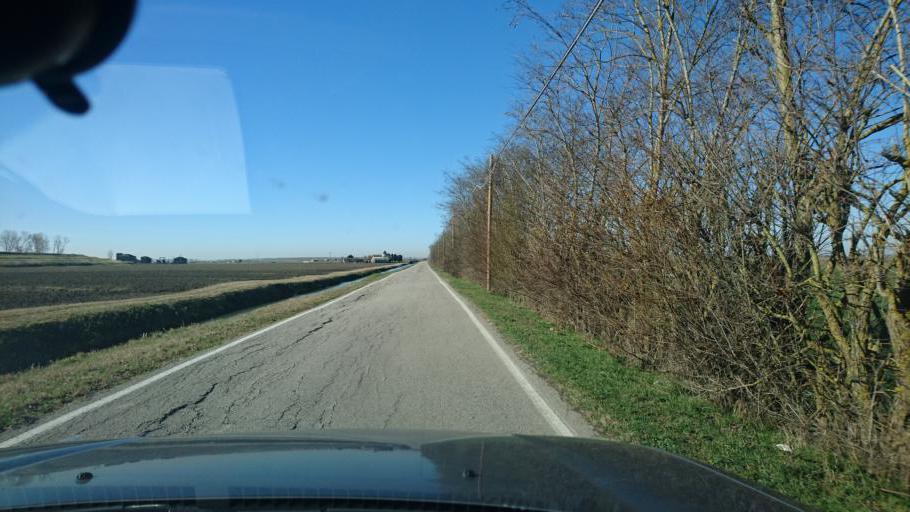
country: IT
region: Veneto
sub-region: Provincia di Rovigo
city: Papozze
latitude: 44.9453
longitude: 12.1731
